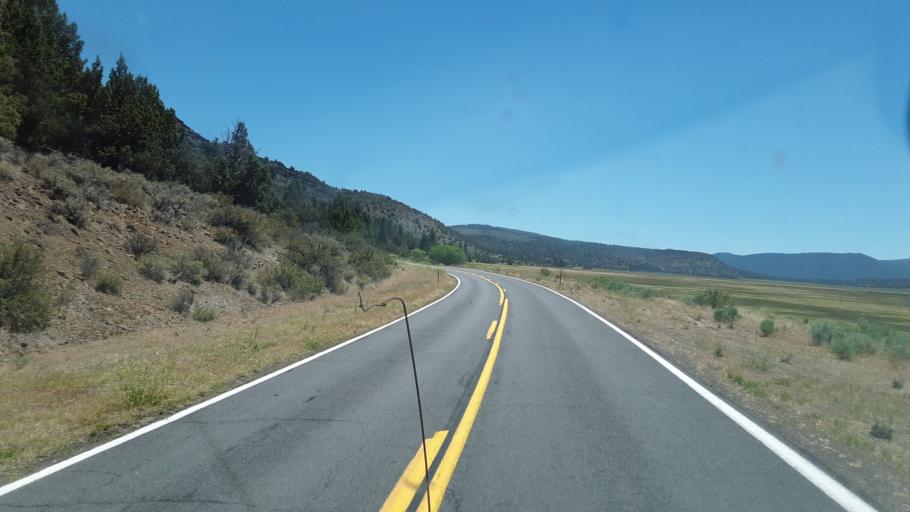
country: US
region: California
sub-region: Lassen County
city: Susanville
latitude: 40.6743
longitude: -120.6576
